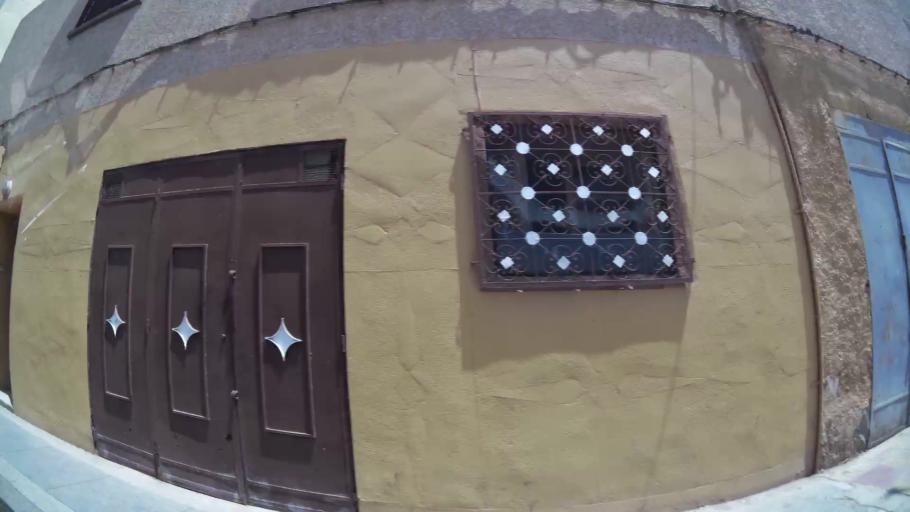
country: MA
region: Oriental
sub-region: Oujda-Angad
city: Oujda
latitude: 34.6847
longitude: -1.9016
